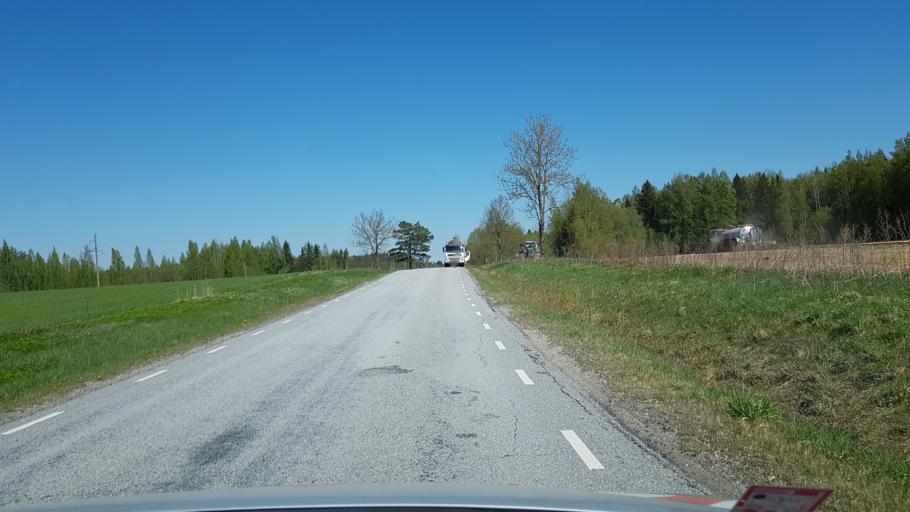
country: EE
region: Vorumaa
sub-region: Voru linn
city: Voru
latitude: 57.9284
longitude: 26.9513
